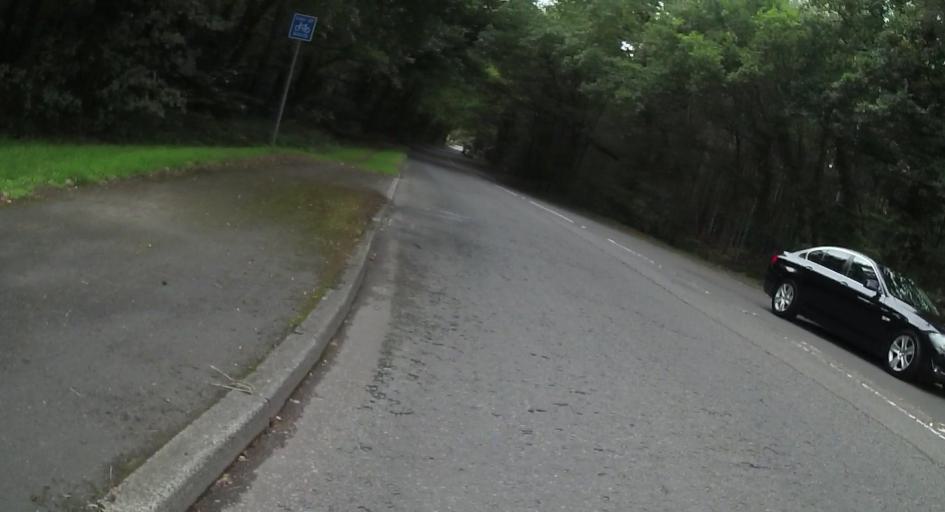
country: GB
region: England
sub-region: Surrey
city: Woking
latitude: 51.3331
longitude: -0.5464
